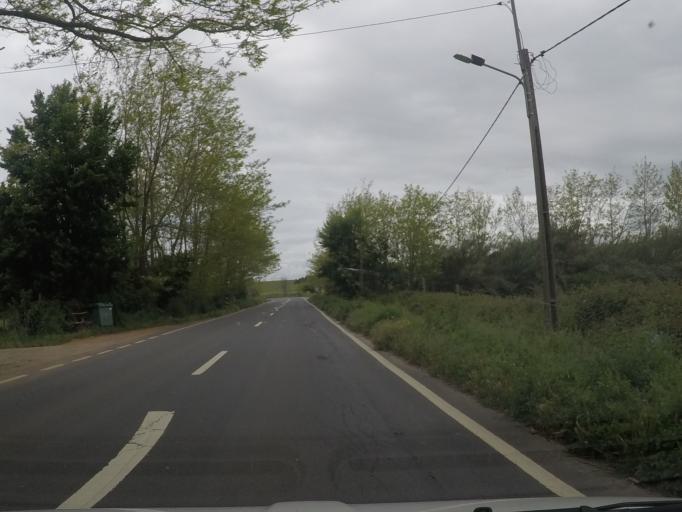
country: PT
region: Setubal
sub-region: Santiago do Cacem
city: Cercal
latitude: 37.8195
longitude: -8.6838
